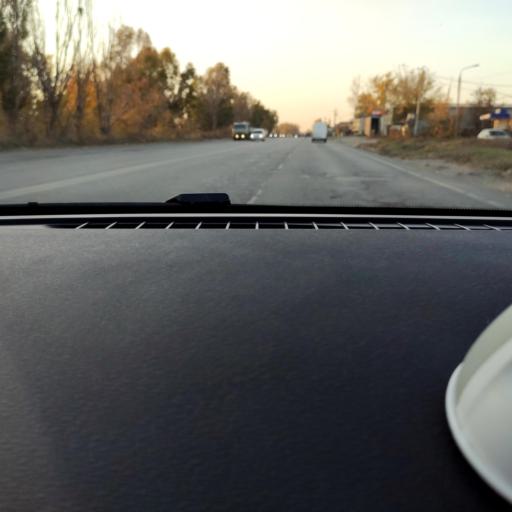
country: RU
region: Samara
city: Petra-Dubrava
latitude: 53.2623
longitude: 50.2890
